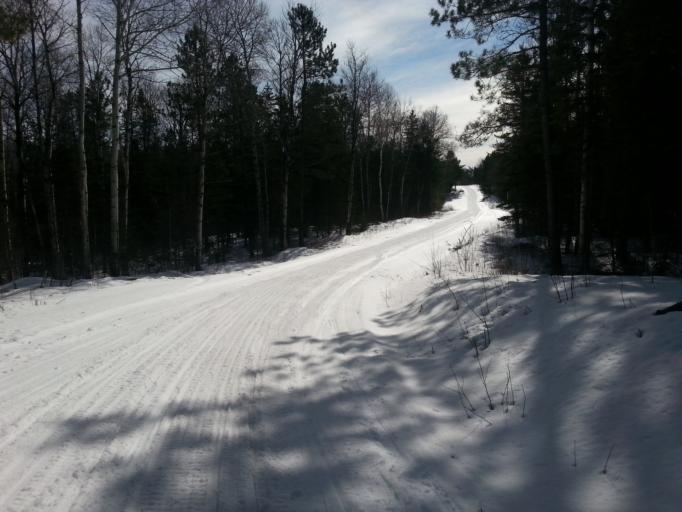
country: CA
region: Ontario
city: Greater Sudbury
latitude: 46.3397
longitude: -80.9019
